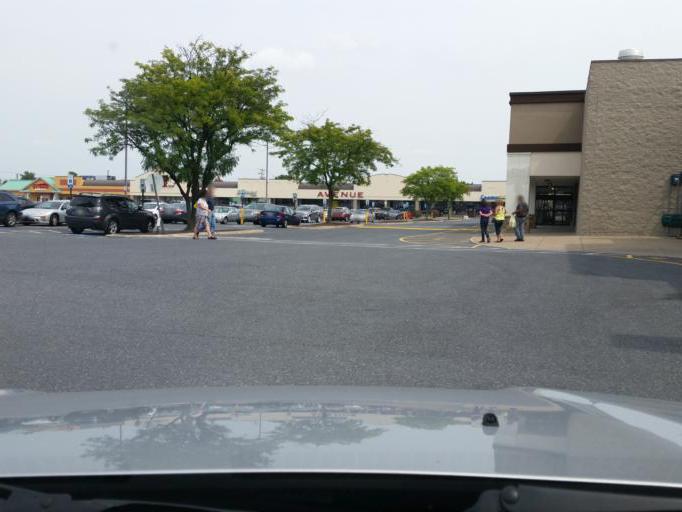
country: US
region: Pennsylvania
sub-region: Cumberland County
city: Shiremanstown
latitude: 40.2366
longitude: -76.9806
